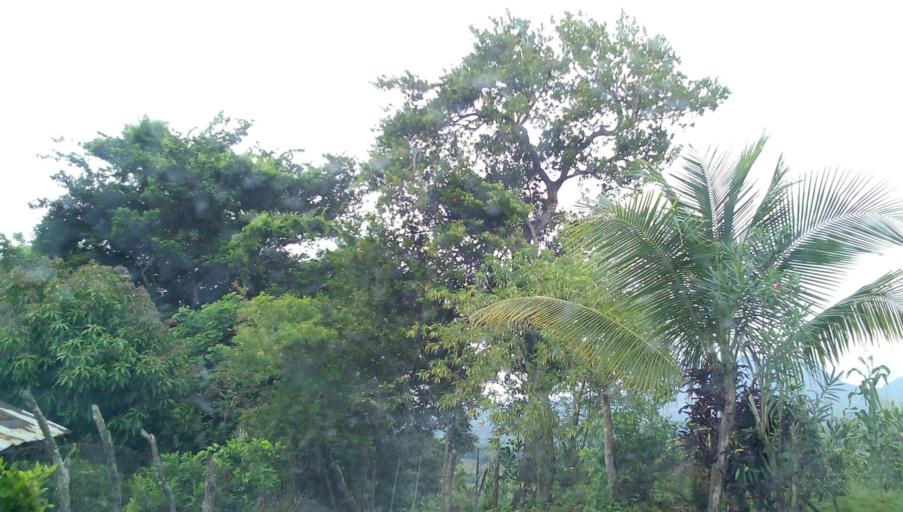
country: MX
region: Veracruz
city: Tepetzintla
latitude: 21.1287
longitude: -97.8586
